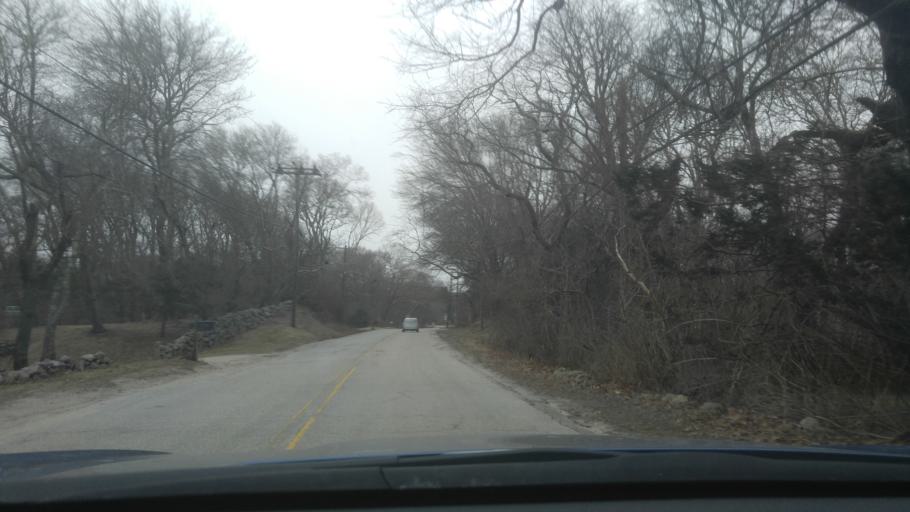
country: US
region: Rhode Island
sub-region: Washington County
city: Wakefield-Peacedale
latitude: 41.4140
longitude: -71.5285
